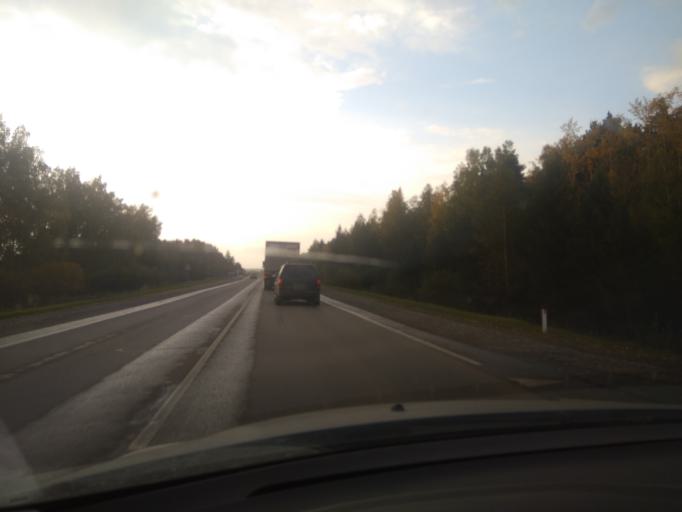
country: RU
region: Sverdlovsk
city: Verkhneye Dubrovo
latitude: 56.7237
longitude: 61.0443
